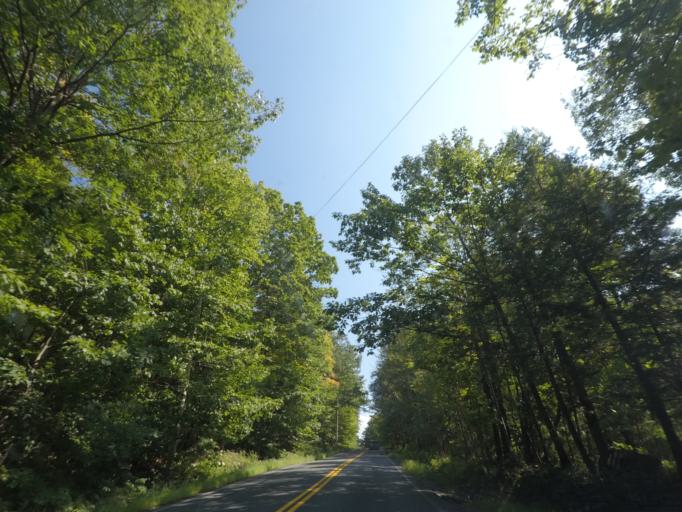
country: US
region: New York
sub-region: Rensselaer County
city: Poestenkill
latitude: 42.7373
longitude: -73.5116
